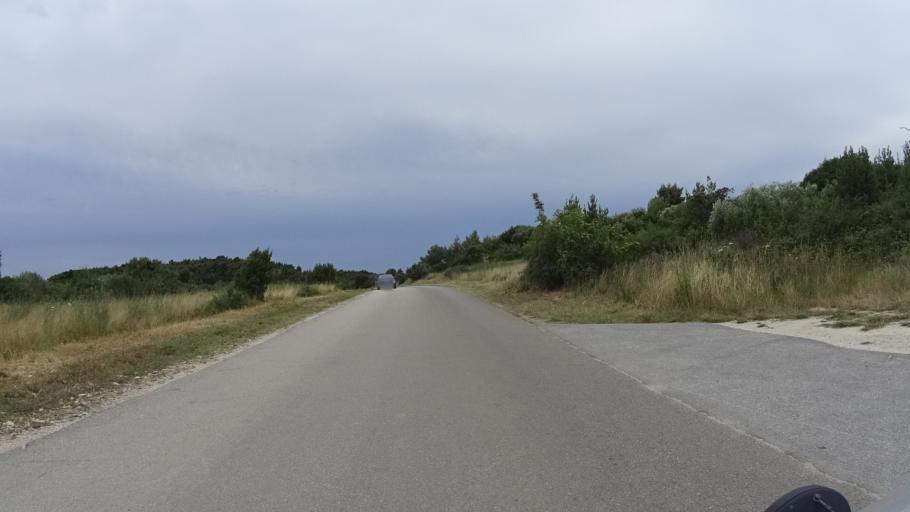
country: HR
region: Istarska
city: Medulin
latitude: 44.8002
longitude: 13.9060
